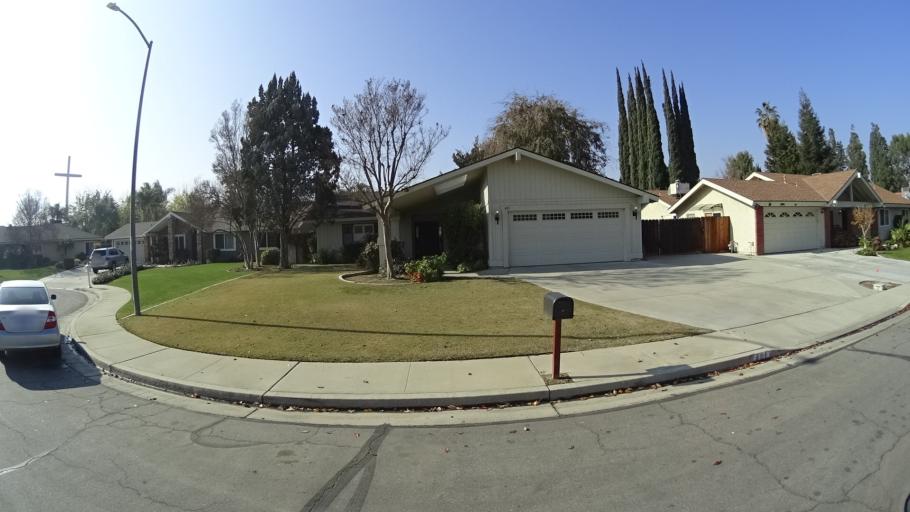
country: US
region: California
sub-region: Kern County
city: Greenacres
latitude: 35.3564
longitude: -119.0801
